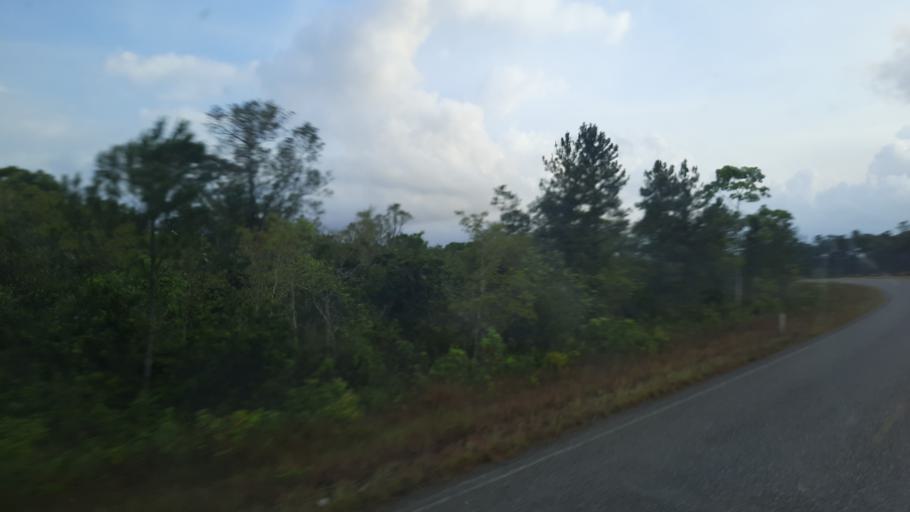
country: BZ
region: Stann Creek
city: Placencia
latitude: 16.6785
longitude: -88.4383
